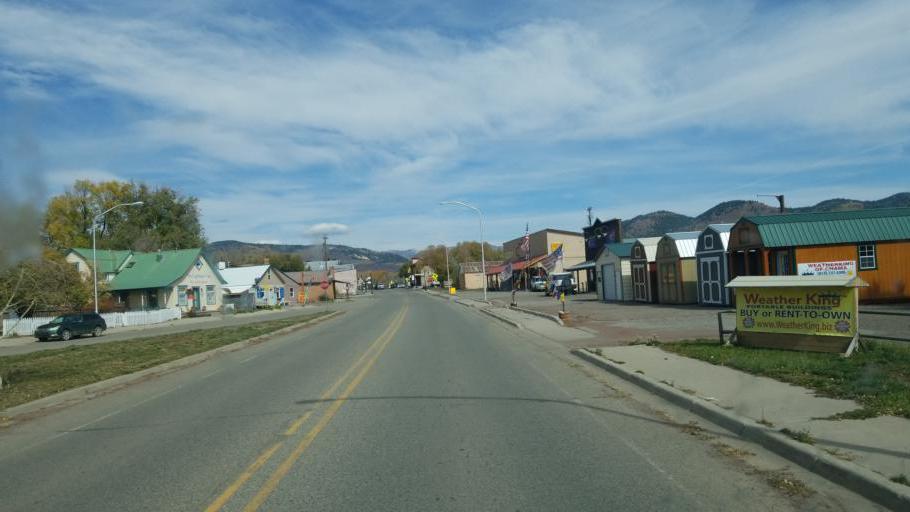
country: US
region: New Mexico
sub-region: Rio Arriba County
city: Chama
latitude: 36.9007
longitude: -106.5802
